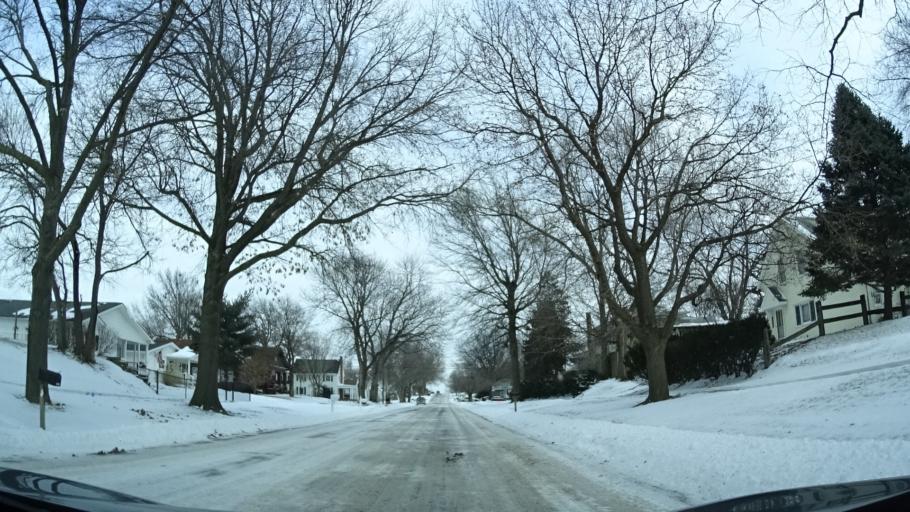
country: US
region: Nebraska
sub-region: Otoe County
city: Nebraska City
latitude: 40.6758
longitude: -95.8627
